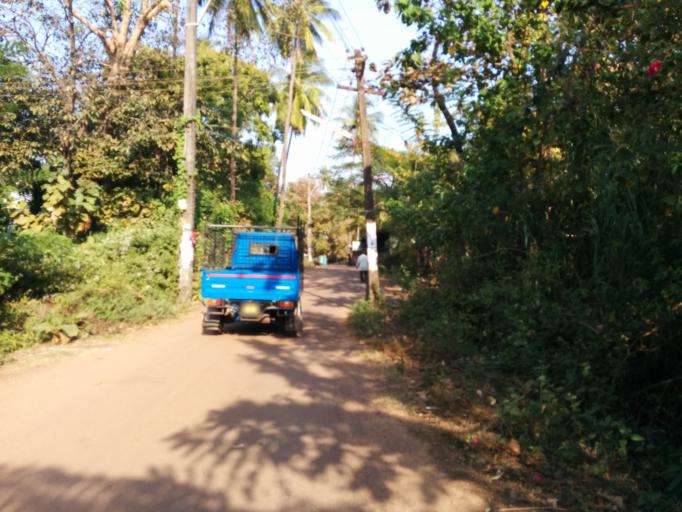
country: IN
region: Karnataka
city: Canacona
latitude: 15.0036
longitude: 74.0295
